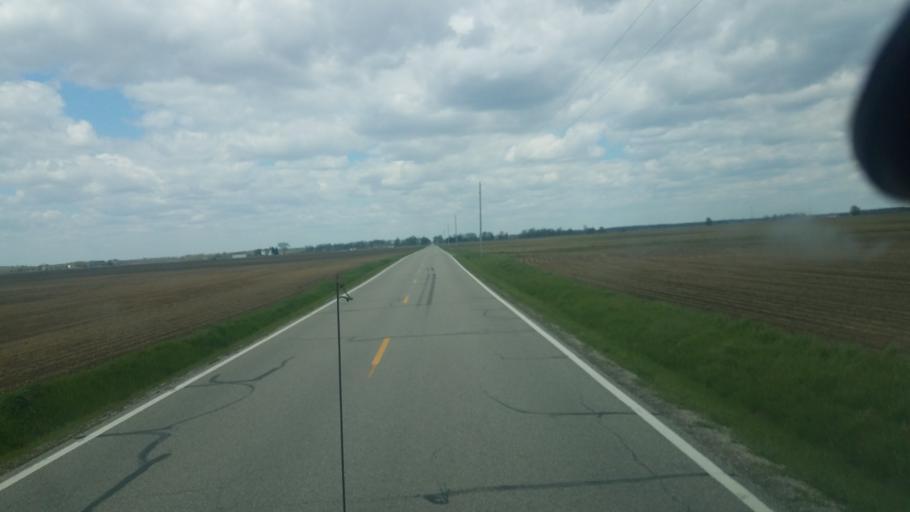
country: US
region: Ohio
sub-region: Marion County
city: Marion
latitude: 40.7091
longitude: -83.0923
